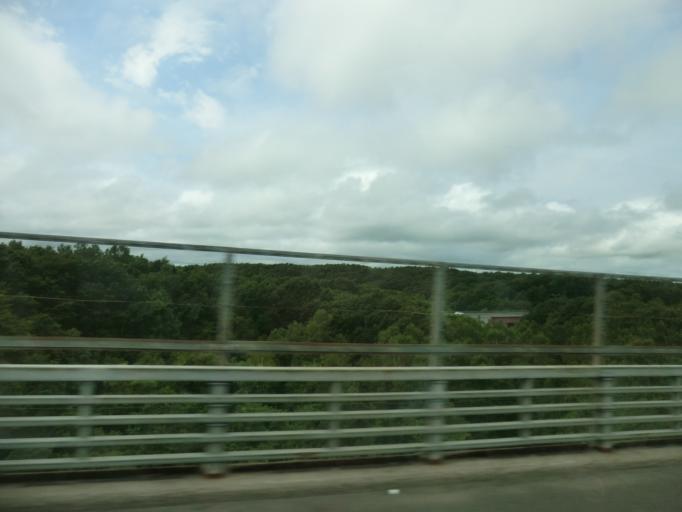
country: JP
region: Hokkaido
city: Kitahiroshima
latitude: 42.9138
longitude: 141.5486
